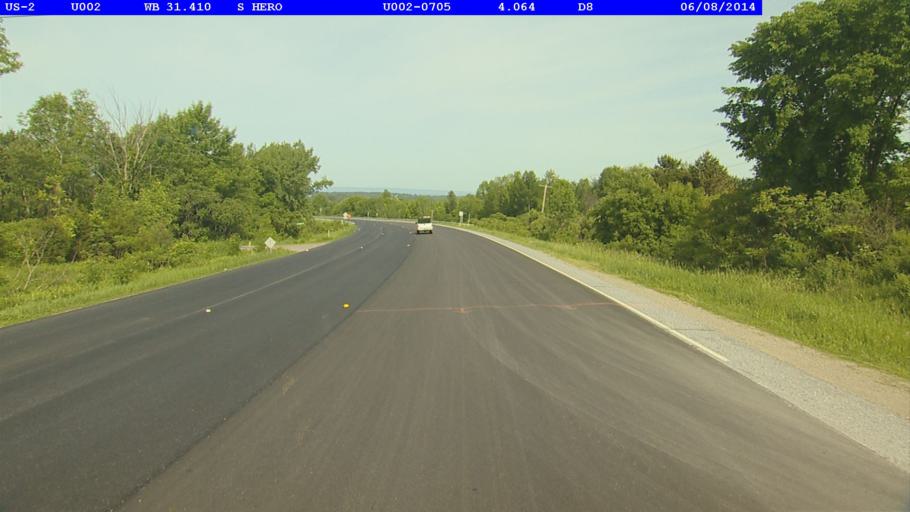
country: US
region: New York
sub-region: Clinton County
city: Cumberland Head
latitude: 44.6460
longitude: -73.2831
